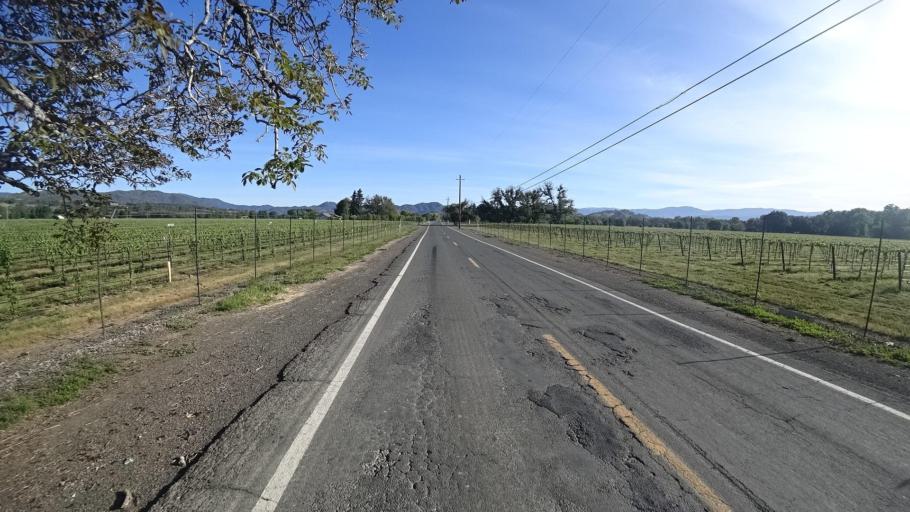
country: US
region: California
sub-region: Lake County
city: Lakeport
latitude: 39.0671
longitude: -122.9498
